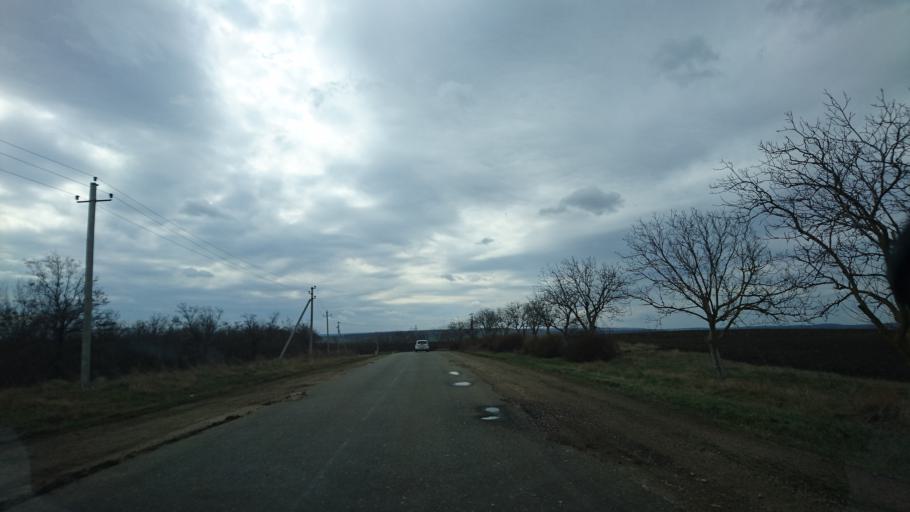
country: MD
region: Cantemir
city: Visniovca
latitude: 46.3225
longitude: 28.5290
